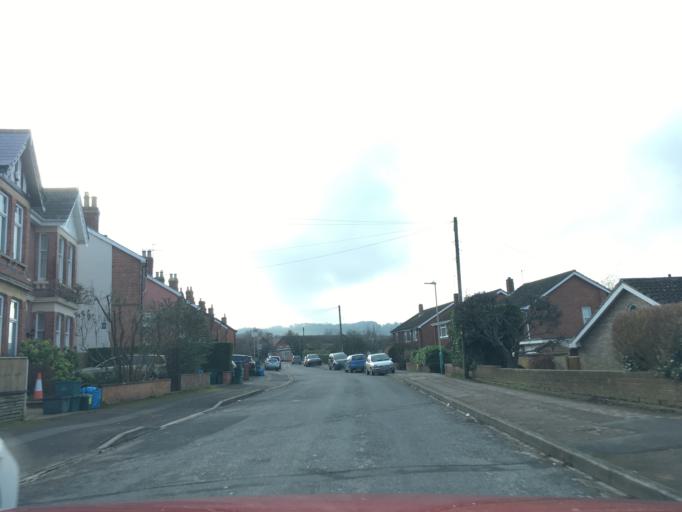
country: GB
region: England
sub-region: Gloucestershire
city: Cheltenham
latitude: 51.8788
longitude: -2.0793
